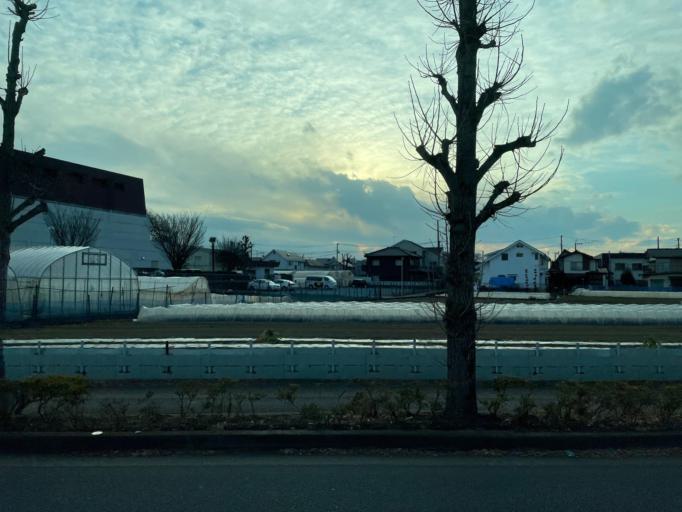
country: JP
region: Tokyo
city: Tanashicho
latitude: 35.7564
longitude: 139.5226
